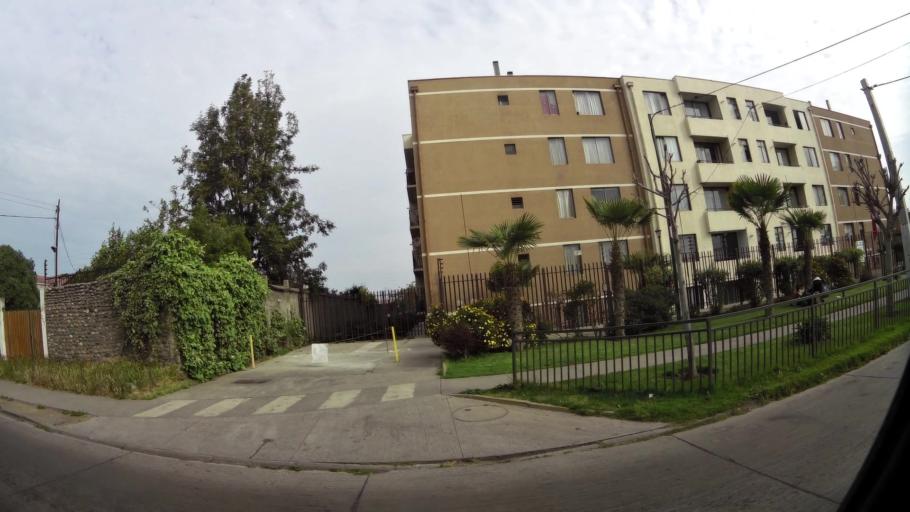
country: CL
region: Santiago Metropolitan
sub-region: Provincia de Santiago
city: Lo Prado
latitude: -33.5161
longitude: -70.7525
